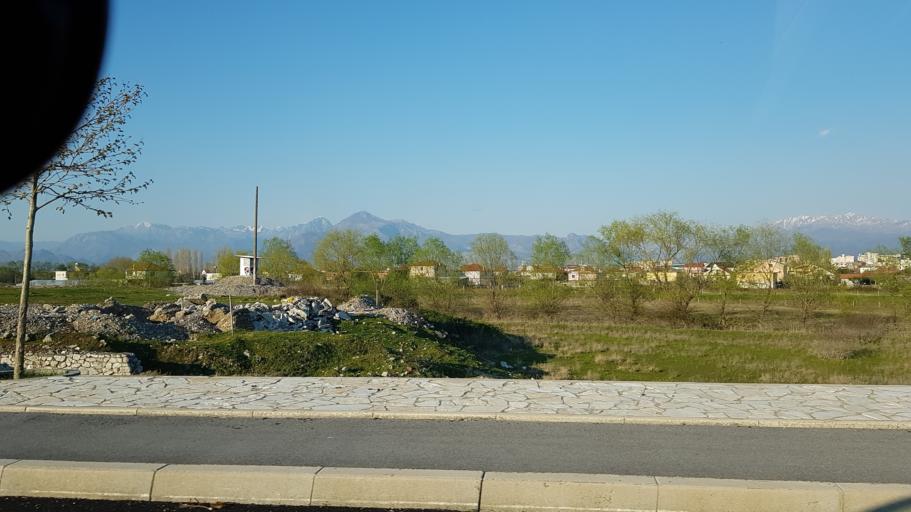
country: AL
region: Shkoder
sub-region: Rrethi i Shkodres
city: Shkoder
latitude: 42.0636
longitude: 19.4923
